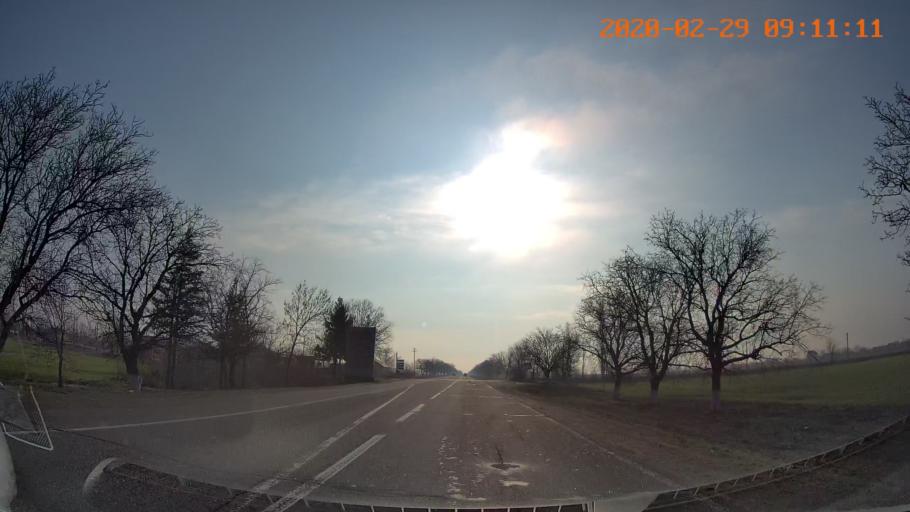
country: MD
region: Telenesti
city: Slobozia
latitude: 46.8374
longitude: 29.7953
